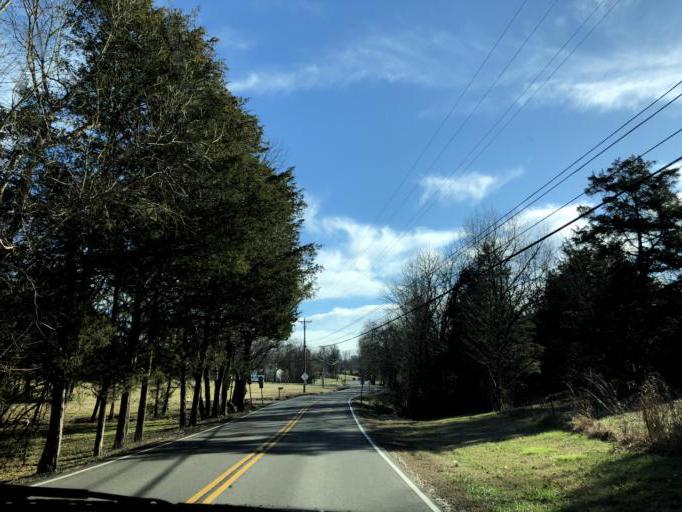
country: US
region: Tennessee
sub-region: Wilson County
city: Green Hill
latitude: 36.1717
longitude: -86.5643
